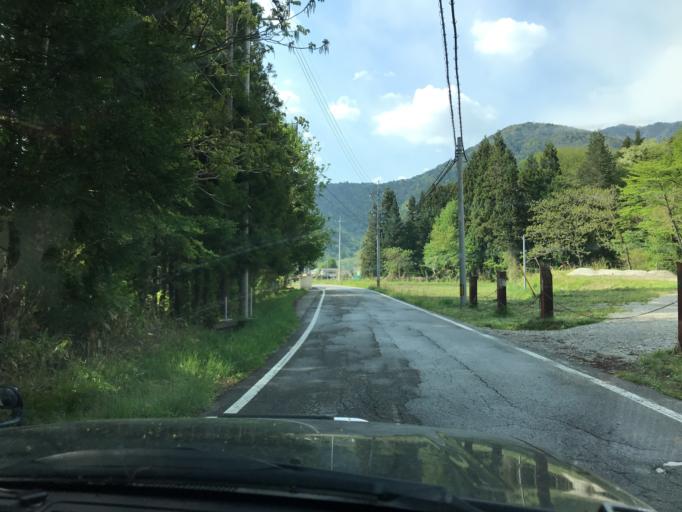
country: JP
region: Nagano
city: Omachi
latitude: 36.5196
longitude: 137.8133
